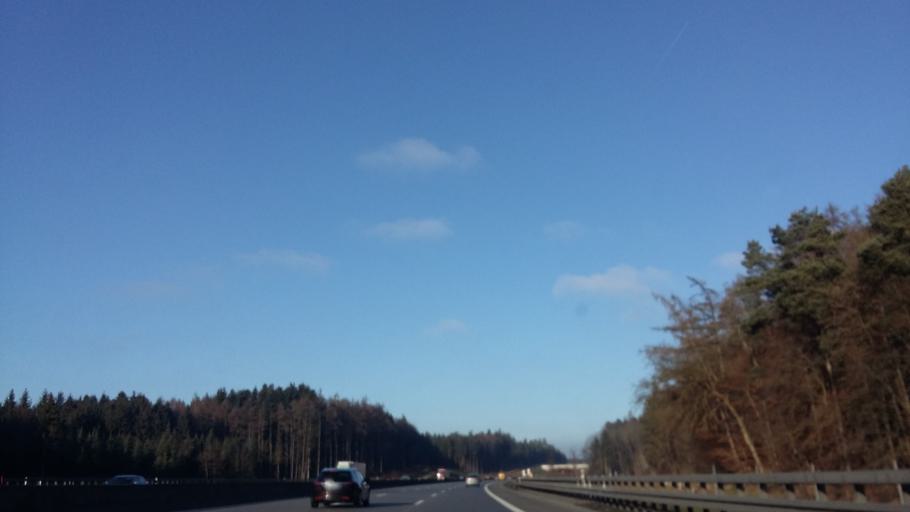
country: DE
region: Bavaria
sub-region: Upper Bavaria
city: Odelzhausen
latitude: 48.3291
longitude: 11.1683
